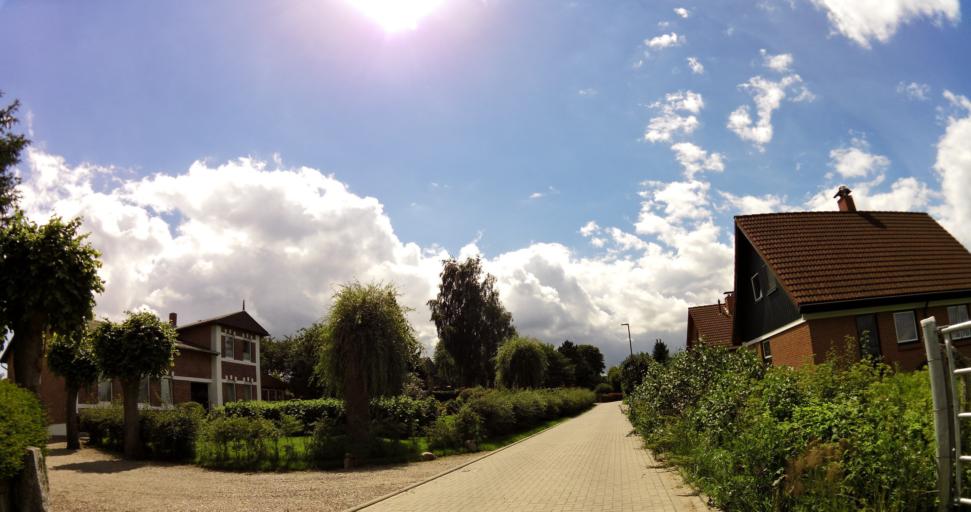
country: DE
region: Schleswig-Holstein
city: Fleckeby
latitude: 54.4852
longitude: 9.7141
